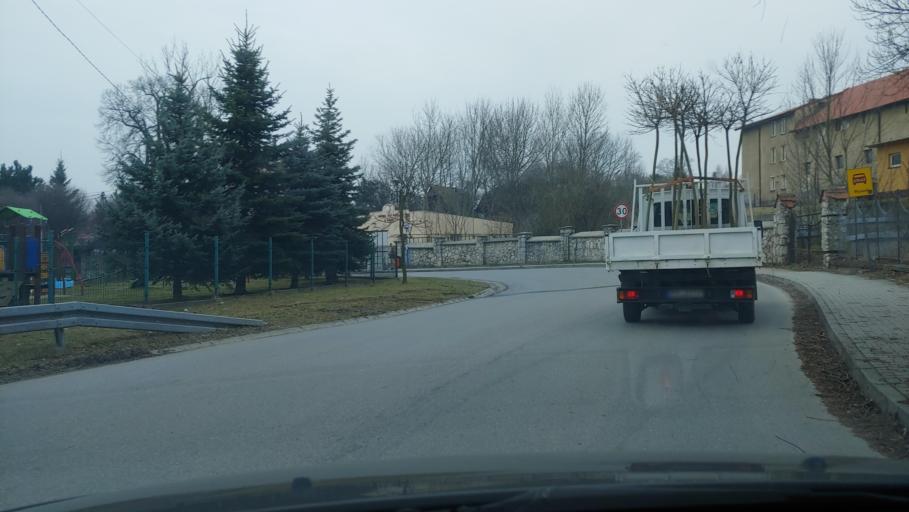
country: PL
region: Lesser Poland Voivodeship
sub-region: Powiat krakowski
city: Balice
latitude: 50.0873
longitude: 19.7910
